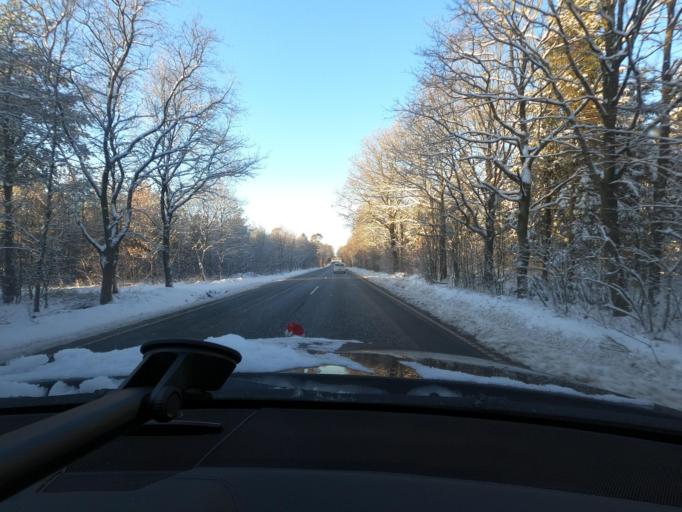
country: DK
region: South Denmark
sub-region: Tonder Kommune
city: Logumkloster
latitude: 55.1781
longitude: 8.9303
